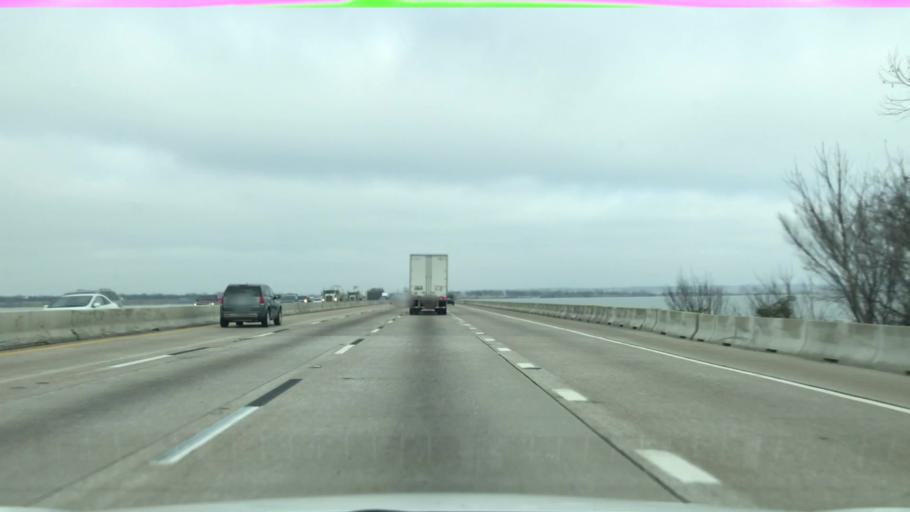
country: US
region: Texas
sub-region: Dallas County
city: Rowlett
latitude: 32.8677
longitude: -96.5380
